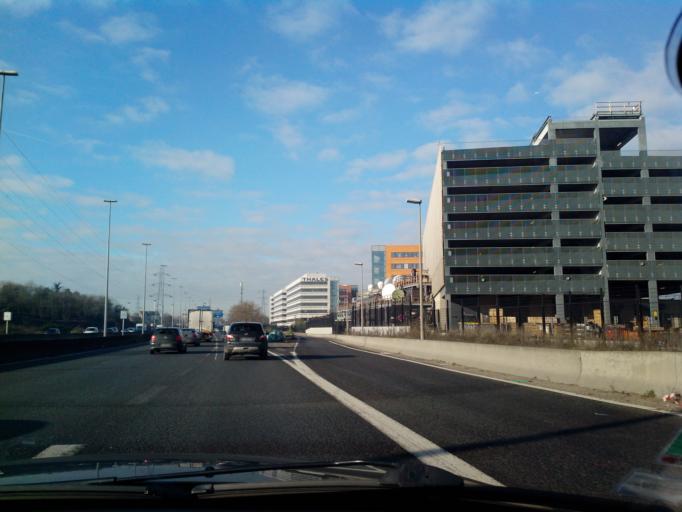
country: FR
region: Ile-de-France
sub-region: Departement des Hauts-de-Seine
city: Villeneuve-la-Garenne
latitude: 48.9384
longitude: 2.3135
